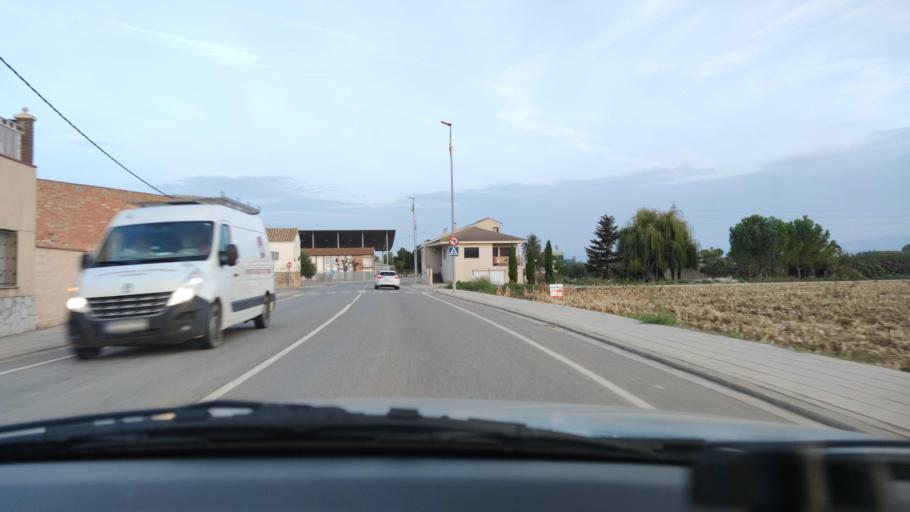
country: ES
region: Catalonia
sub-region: Provincia de Lleida
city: Mollerussa
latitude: 41.6351
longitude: 0.8758
